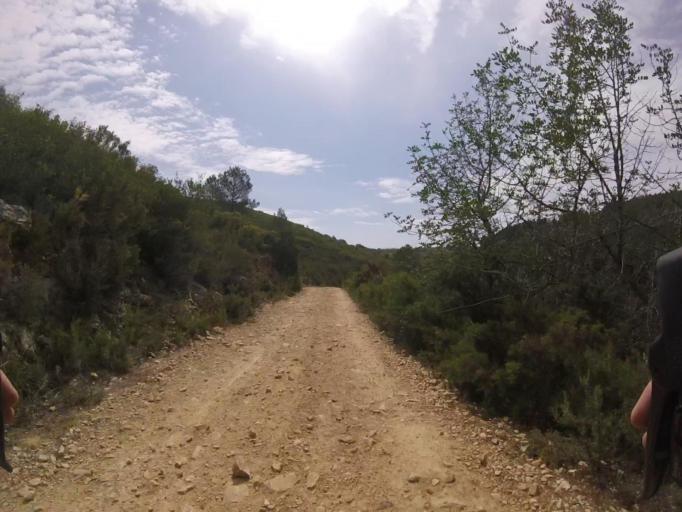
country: ES
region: Valencia
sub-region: Provincia de Castello
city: Cuevas de Vinroma
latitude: 40.2587
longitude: 0.1047
